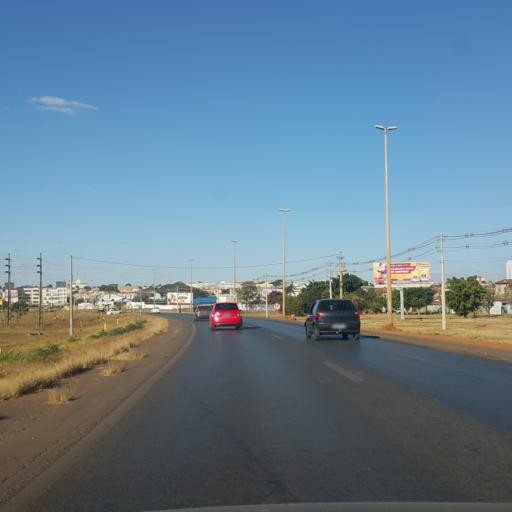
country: BR
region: Federal District
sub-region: Brasilia
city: Brasilia
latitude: -15.8025
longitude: -48.0817
